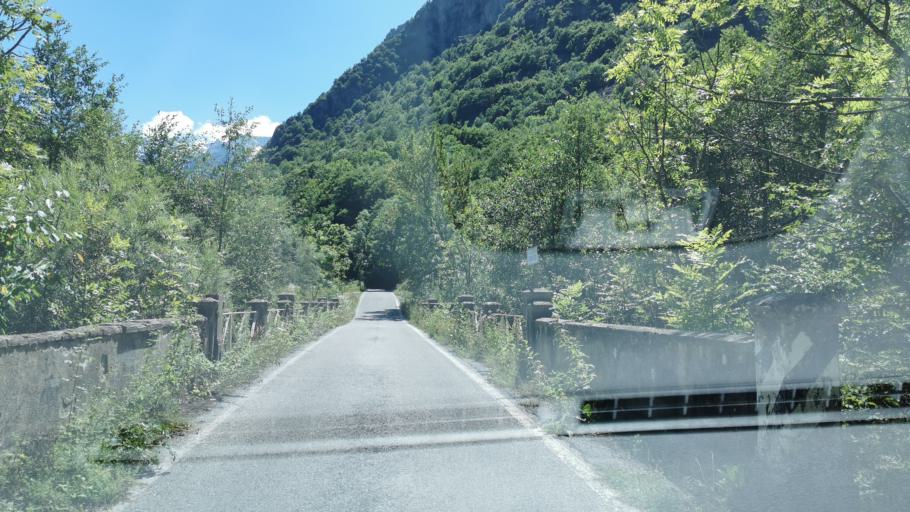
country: IT
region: Piedmont
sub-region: Provincia di Cuneo
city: Entracque
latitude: 44.2066
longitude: 7.3799
